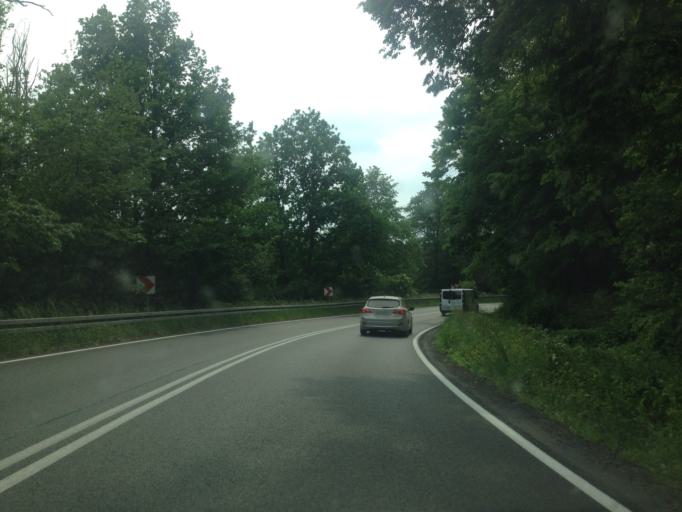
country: PL
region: Kujawsko-Pomorskie
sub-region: Powiat grudziadzki
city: Rogozno
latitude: 53.5062
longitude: 18.9256
